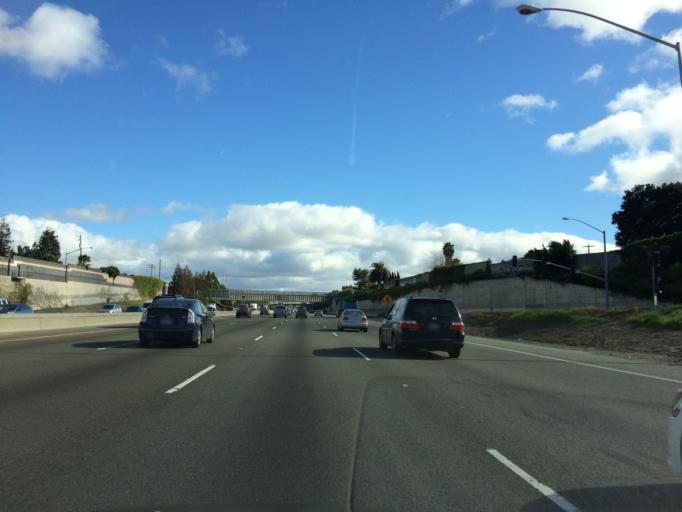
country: US
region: California
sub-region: Alameda County
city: Newark
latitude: 37.5455
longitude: -122.0222
